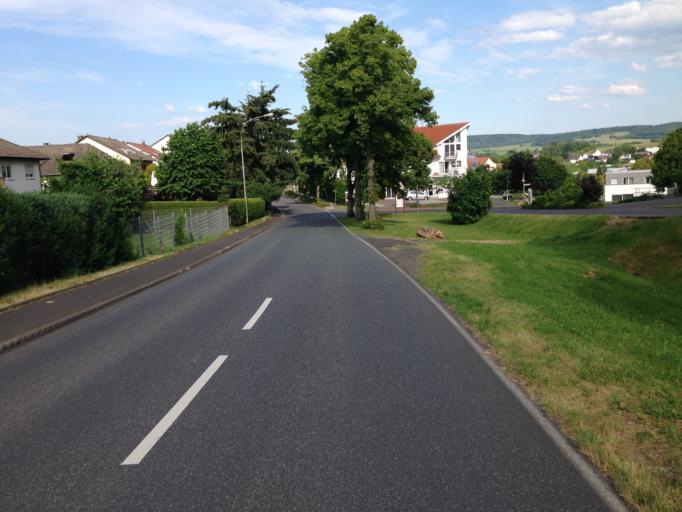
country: DE
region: Hesse
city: Staufenberg
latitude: 50.6601
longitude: 8.7330
